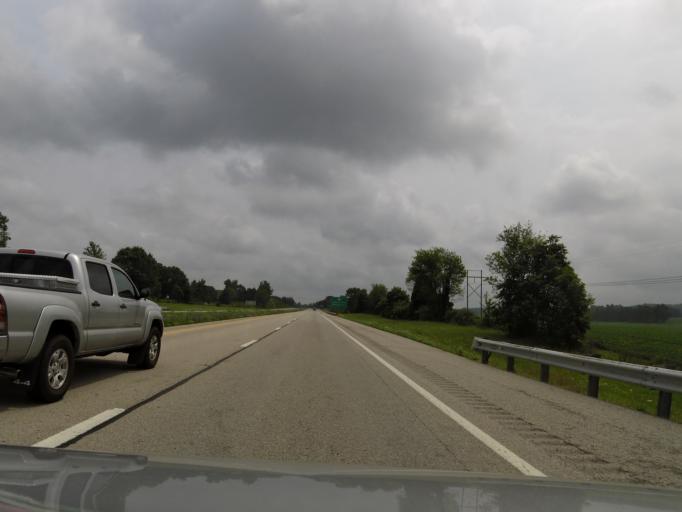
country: US
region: Kentucky
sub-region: Ohio County
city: Beaver Dam
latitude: 37.3590
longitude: -86.8665
